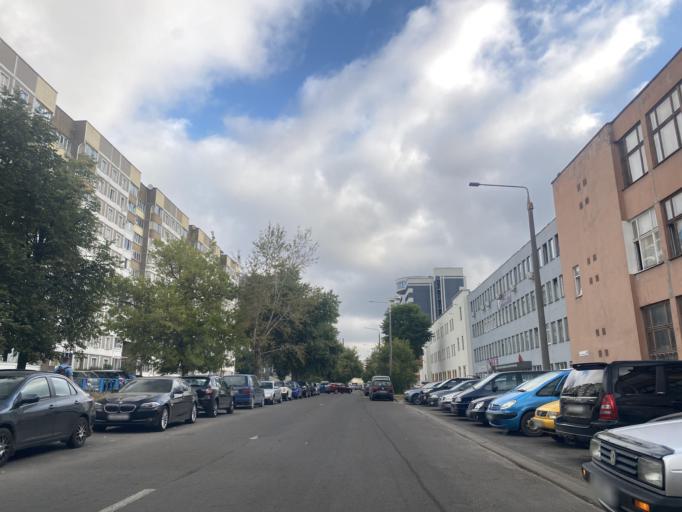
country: BY
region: Minsk
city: Minsk
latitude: 53.9199
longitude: 27.5622
